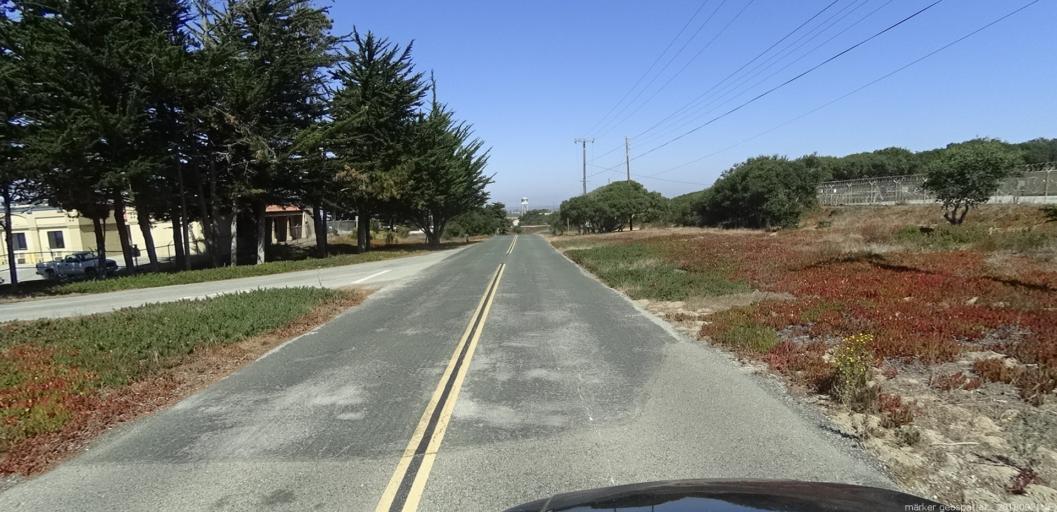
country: US
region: California
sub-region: Monterey County
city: Marina
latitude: 36.6484
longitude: -121.7870
